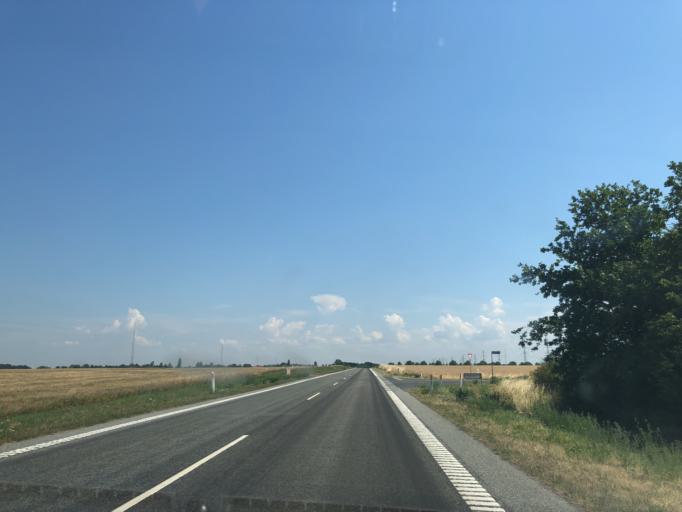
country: DK
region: Zealand
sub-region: Slagelse Kommune
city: Skaelskor
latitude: 55.2153
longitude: 11.2781
